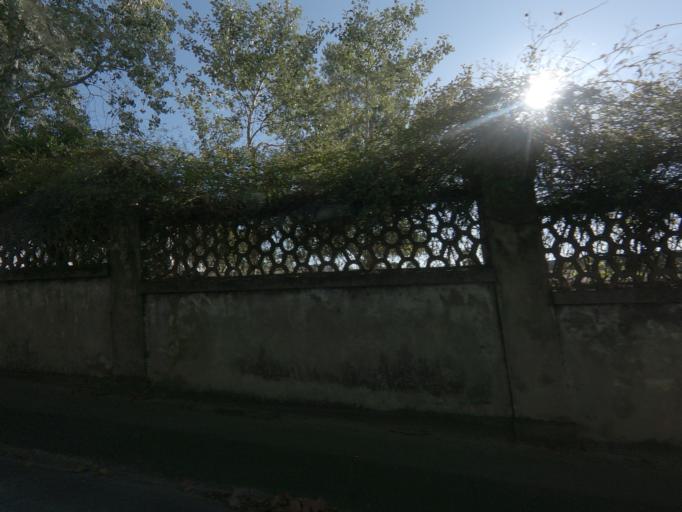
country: PT
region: Setubal
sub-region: Palmela
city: Palmela
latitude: 38.5743
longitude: -8.9062
